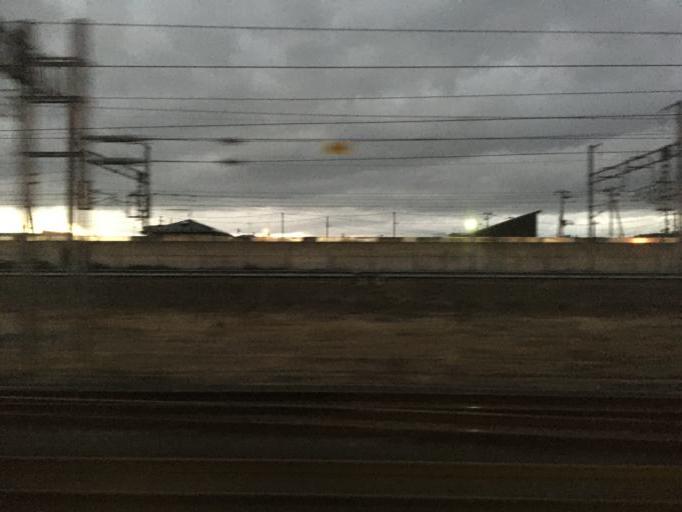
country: JP
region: Aomori
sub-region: Hachinohe Shi
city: Uchimaru
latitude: 40.5120
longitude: 141.4341
